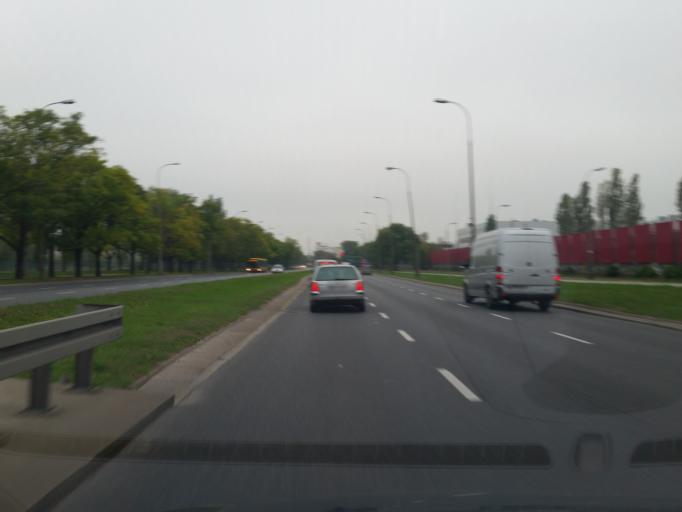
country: PL
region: Masovian Voivodeship
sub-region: Warszawa
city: Zoliborz
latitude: 52.2824
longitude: 21.0098
